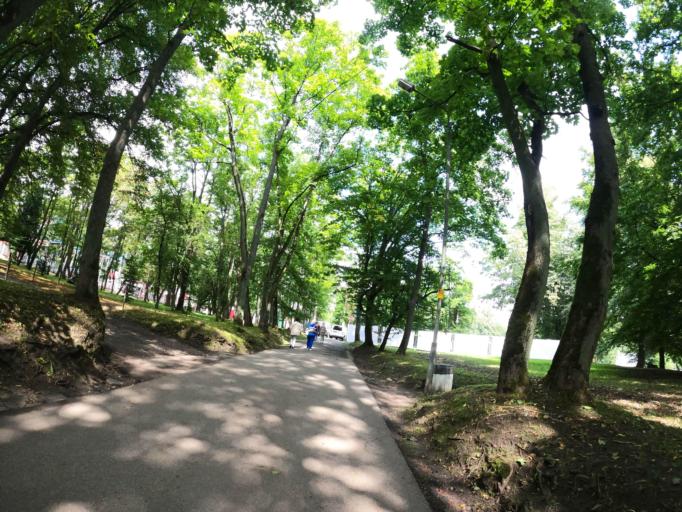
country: RU
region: Kaliningrad
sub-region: Gorod Kaliningrad
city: Kaliningrad
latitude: 54.7165
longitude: 20.4763
